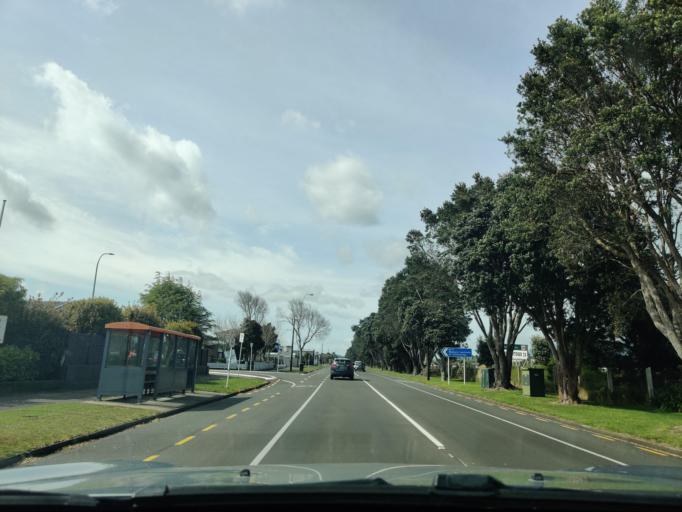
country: NZ
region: Taranaki
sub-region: New Plymouth District
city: New Plymouth
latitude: -39.0626
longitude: 174.0864
